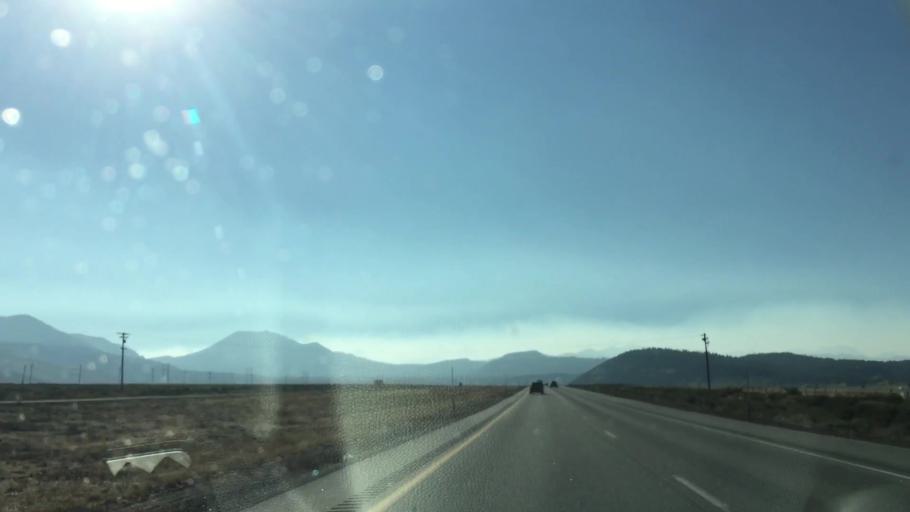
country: US
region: California
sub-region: Mono County
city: Mammoth Lakes
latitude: 37.6237
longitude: -118.8425
